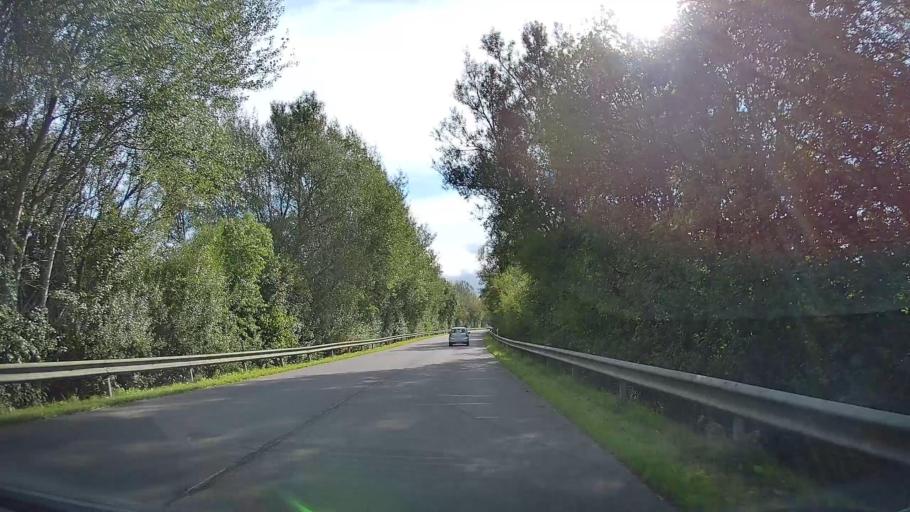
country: DE
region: Schleswig-Holstein
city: Glucksburg
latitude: 54.8495
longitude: 9.5867
